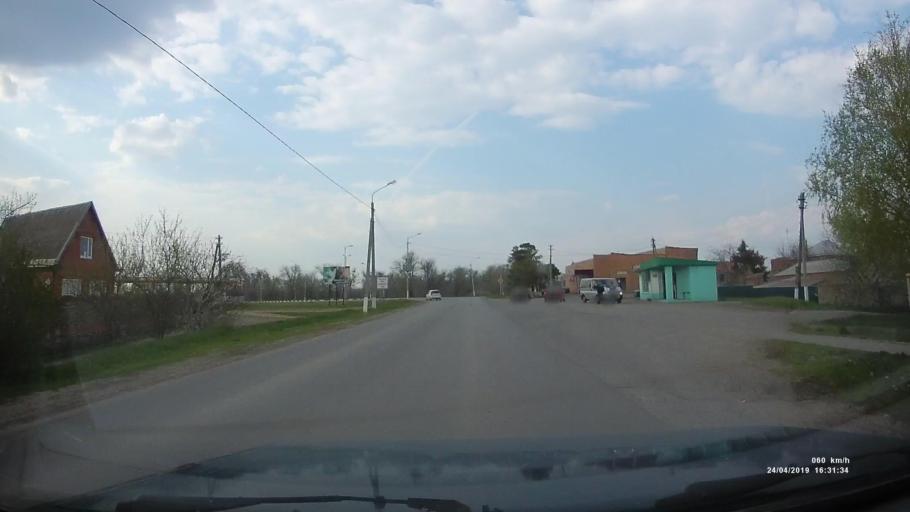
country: RU
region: Rostov
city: Orlovskiy
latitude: 46.8828
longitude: 42.0384
